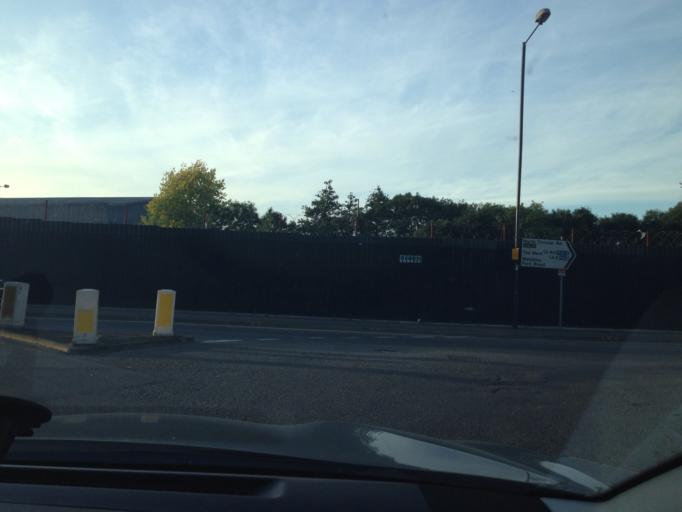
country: GB
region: England
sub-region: Greater London
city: Wembley
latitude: 51.5551
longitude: -0.2595
